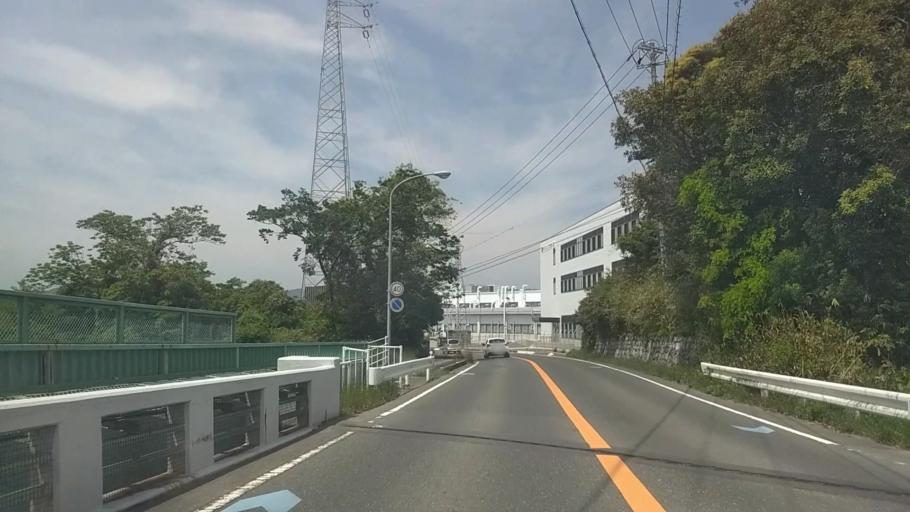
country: JP
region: Shizuoka
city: Kosai-shi
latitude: 34.7215
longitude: 137.5357
